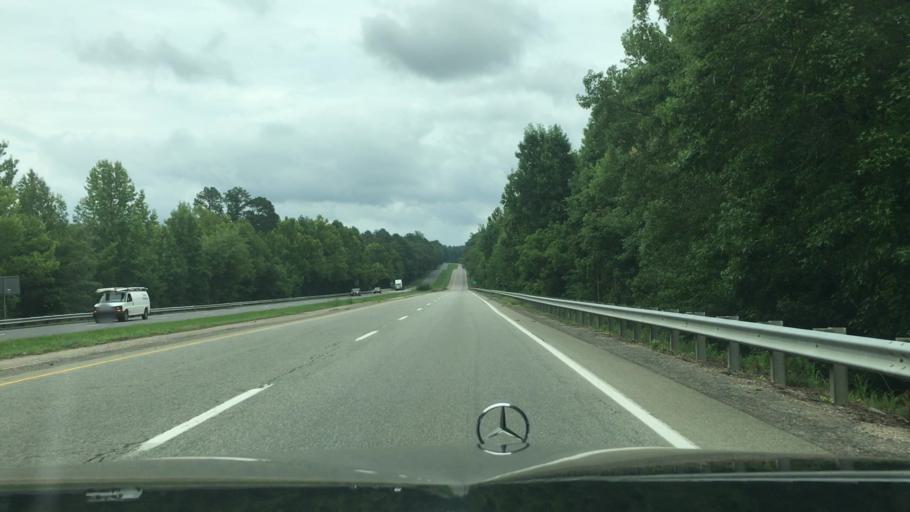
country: US
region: Virginia
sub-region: Amelia County
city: Amelia Court House
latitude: 37.3545
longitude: -77.8554
